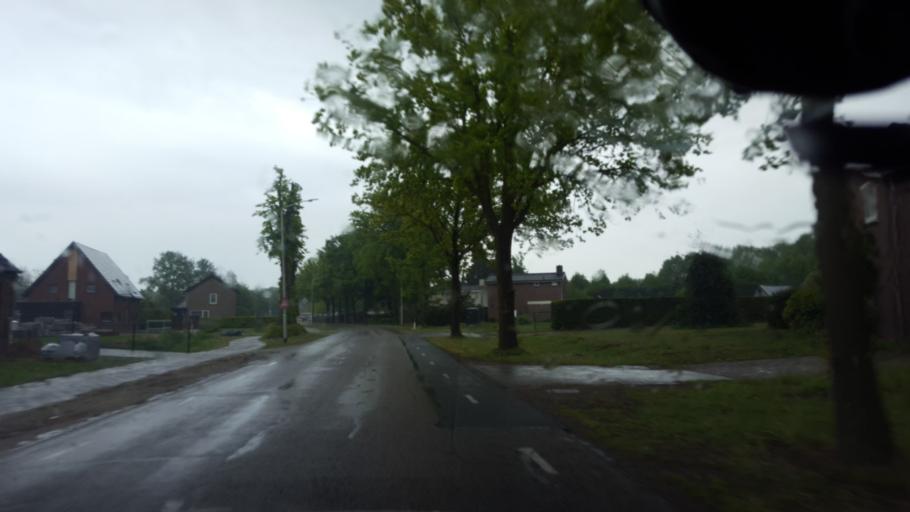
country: NL
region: North Brabant
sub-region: Gemeente Someren
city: Someren
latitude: 51.3905
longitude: 5.6983
